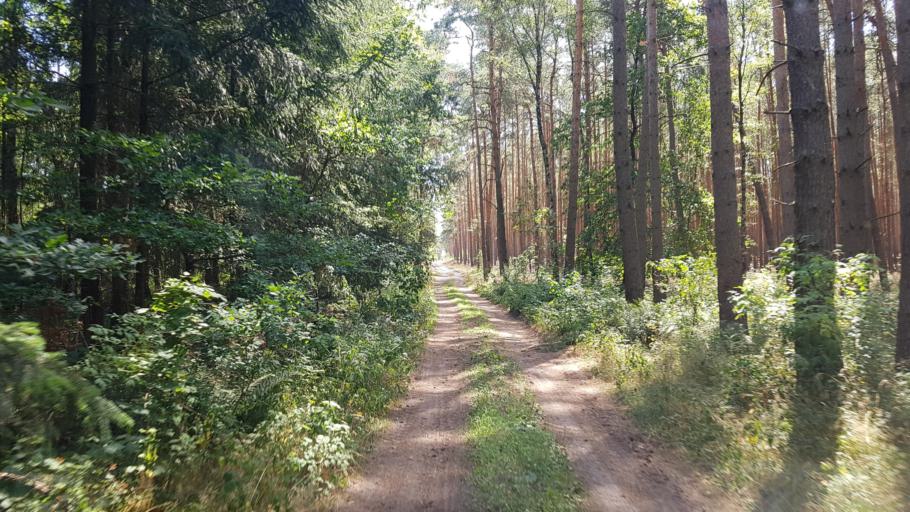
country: DE
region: Brandenburg
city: Finsterwalde
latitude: 51.6646
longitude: 13.7633
